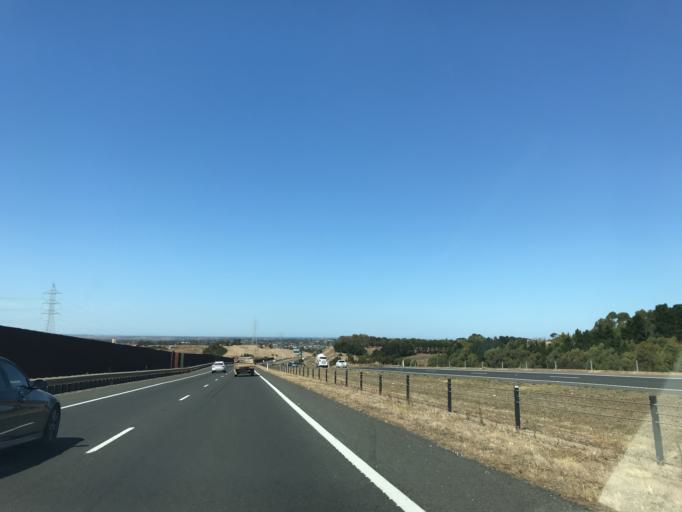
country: AU
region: Victoria
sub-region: Greater Geelong
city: Wandana Heights
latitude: -38.1804
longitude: 144.2991
